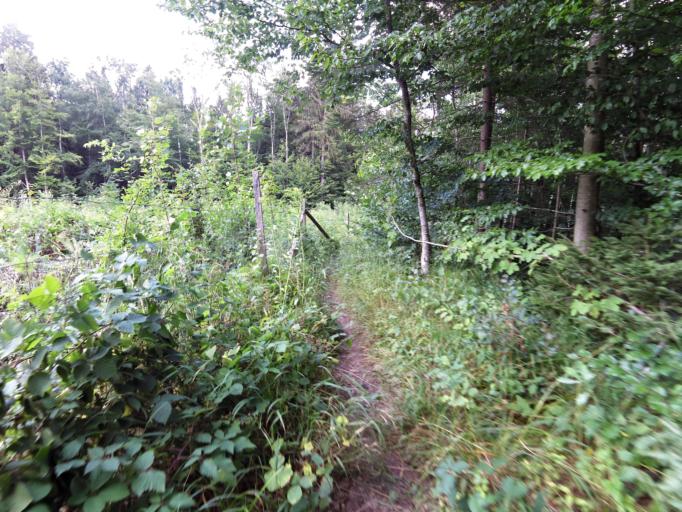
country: CH
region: Thurgau
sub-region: Kreuzlingen District
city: Tagerwilen
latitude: 47.6336
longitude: 9.1399
